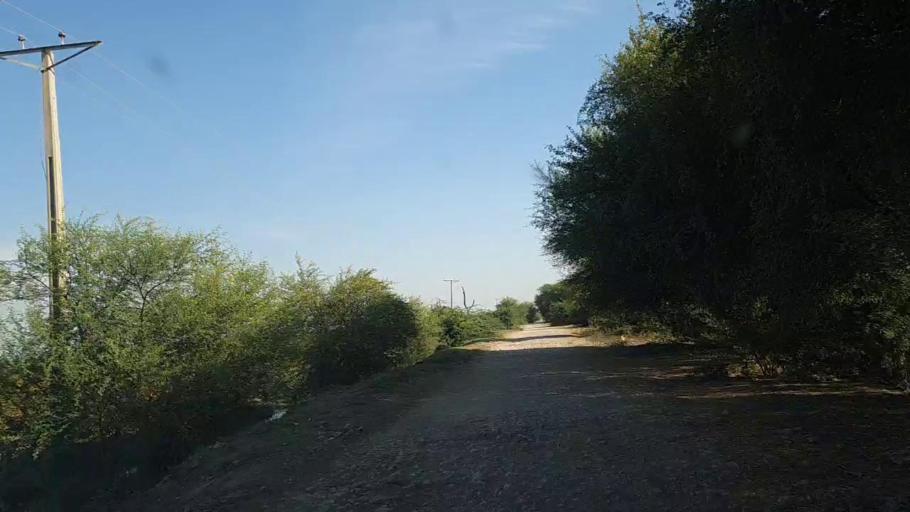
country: PK
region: Sindh
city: Bulri
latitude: 24.8040
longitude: 68.3313
